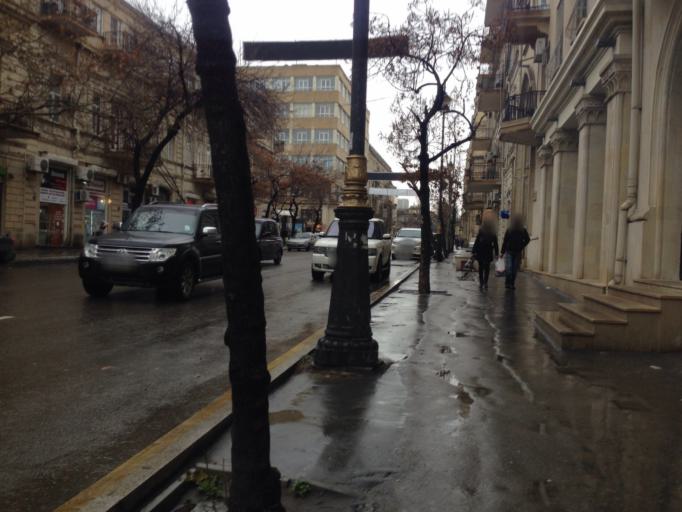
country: AZ
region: Baki
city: Baku
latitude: 40.3771
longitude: 49.8485
